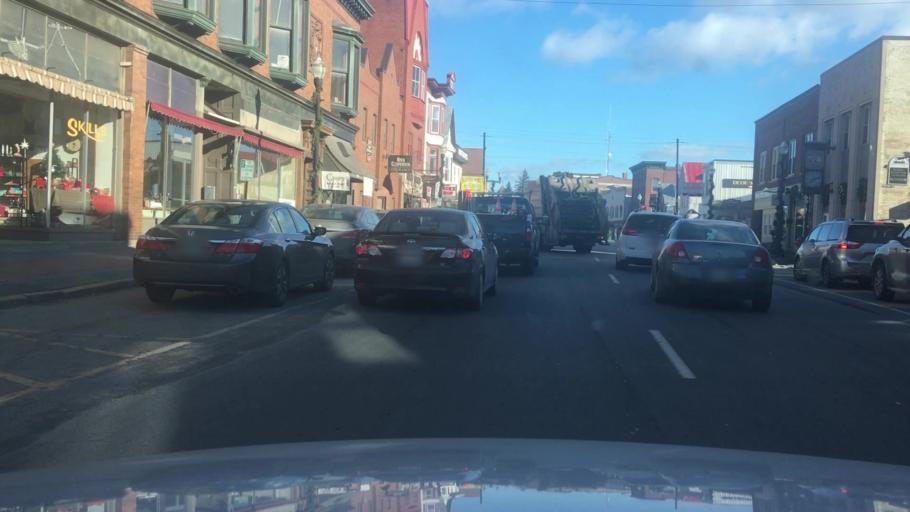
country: US
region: Maine
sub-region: Somerset County
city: Skowhegan
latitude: 44.7653
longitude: -69.7187
